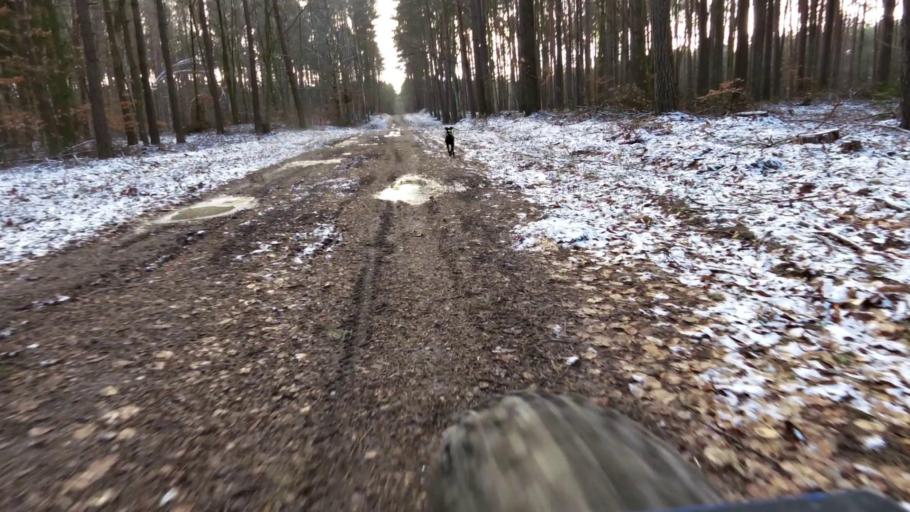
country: PL
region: West Pomeranian Voivodeship
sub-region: Powiat walecki
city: Walcz
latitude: 53.2872
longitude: 16.3037
